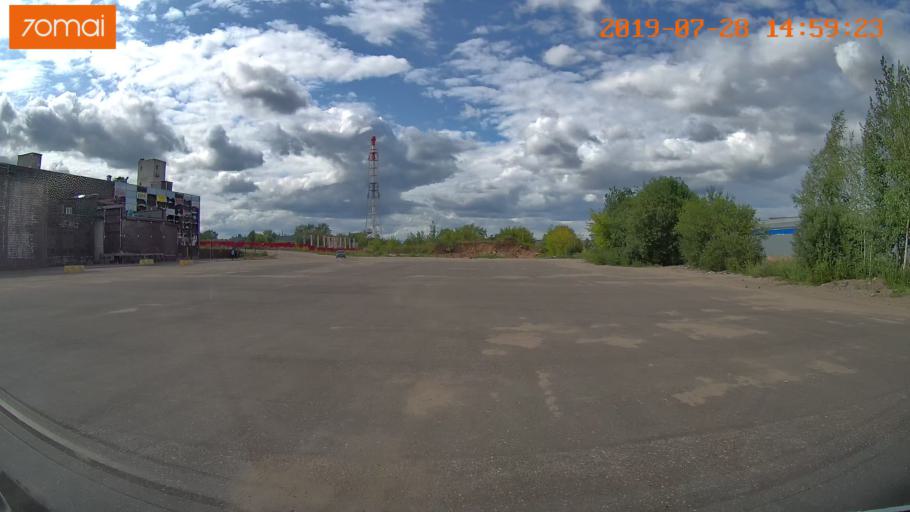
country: RU
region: Ivanovo
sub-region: Gorod Ivanovo
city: Ivanovo
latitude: 56.9682
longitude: 41.0247
